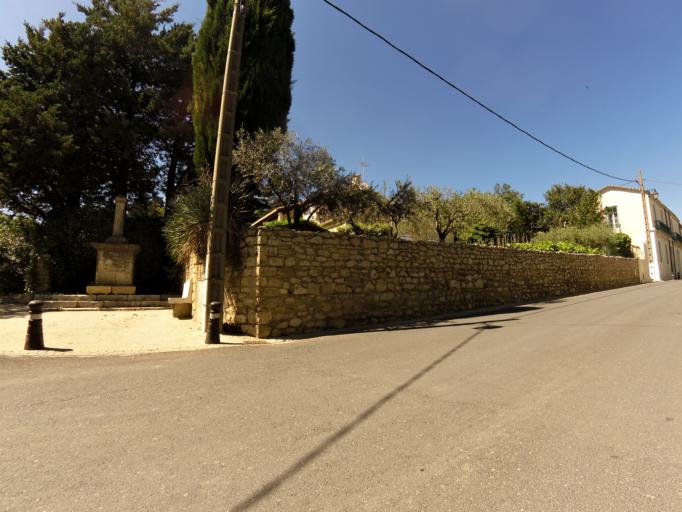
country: FR
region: Languedoc-Roussillon
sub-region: Departement de l'Herault
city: Assas
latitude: 43.7003
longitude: 3.8993
